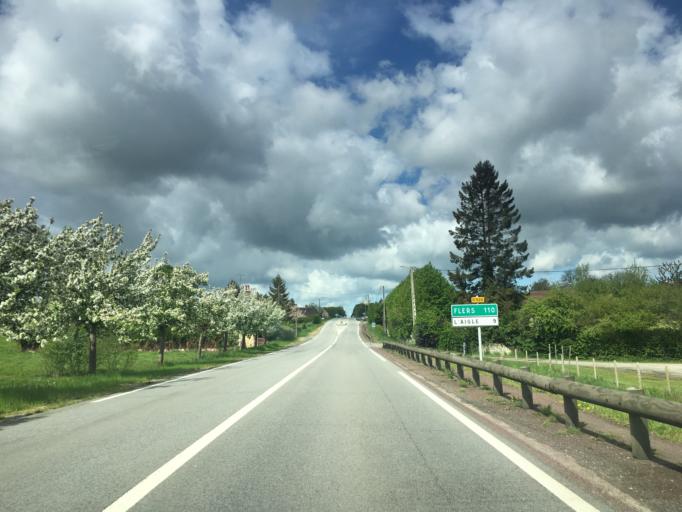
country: FR
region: Haute-Normandie
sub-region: Departement de l'Eure
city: Rugles
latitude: 48.7540
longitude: 0.7310
